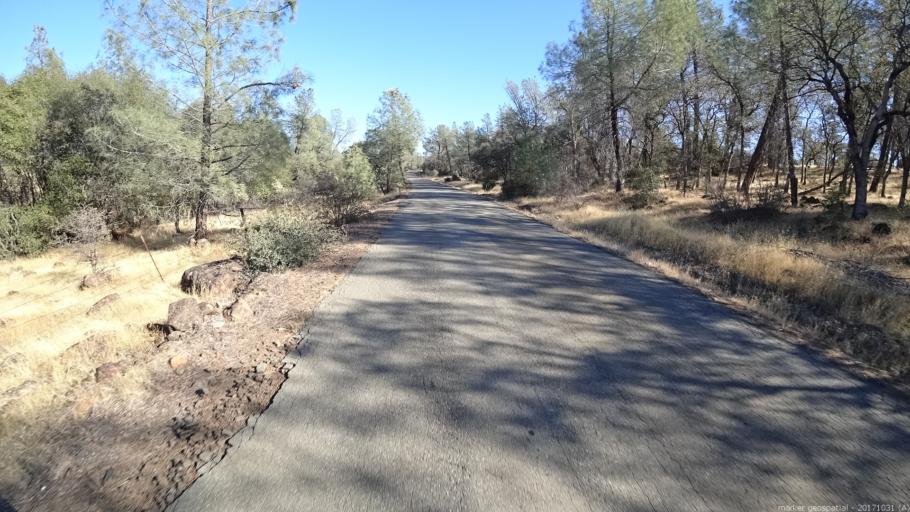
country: US
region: California
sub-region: Shasta County
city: Shingletown
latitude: 40.4598
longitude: -122.0484
